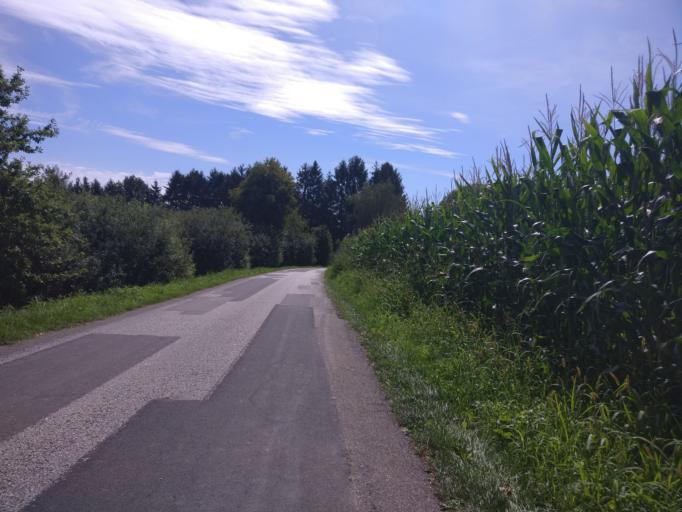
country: AT
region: Styria
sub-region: Politischer Bezirk Hartberg-Fuerstenfeld
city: Blaindorf
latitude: 47.1462
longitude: 15.8842
